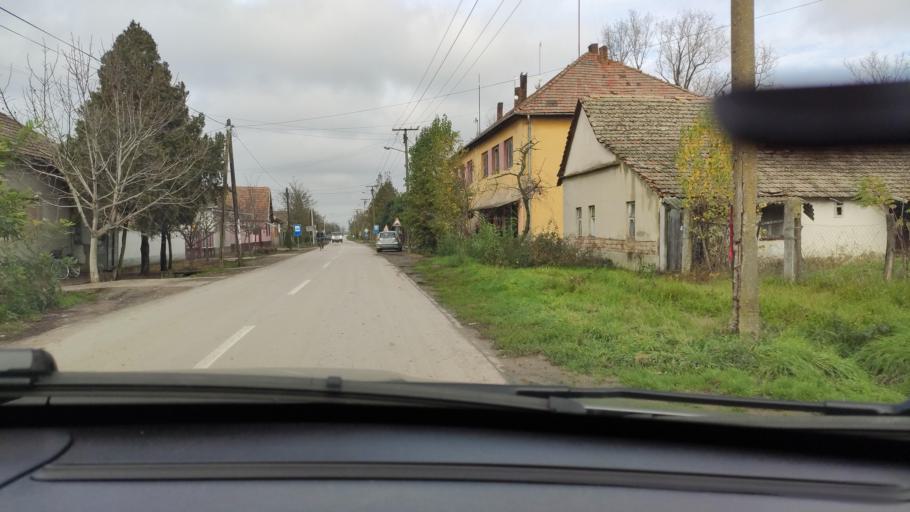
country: RS
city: Jazovo
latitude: 45.8989
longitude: 20.2176
